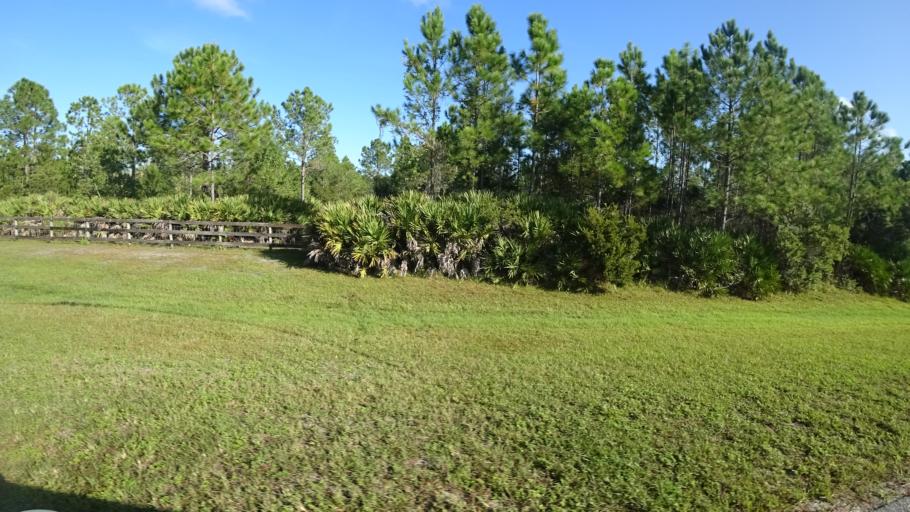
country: US
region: Florida
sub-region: Sarasota County
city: The Meadows
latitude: 27.4243
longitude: -82.3453
